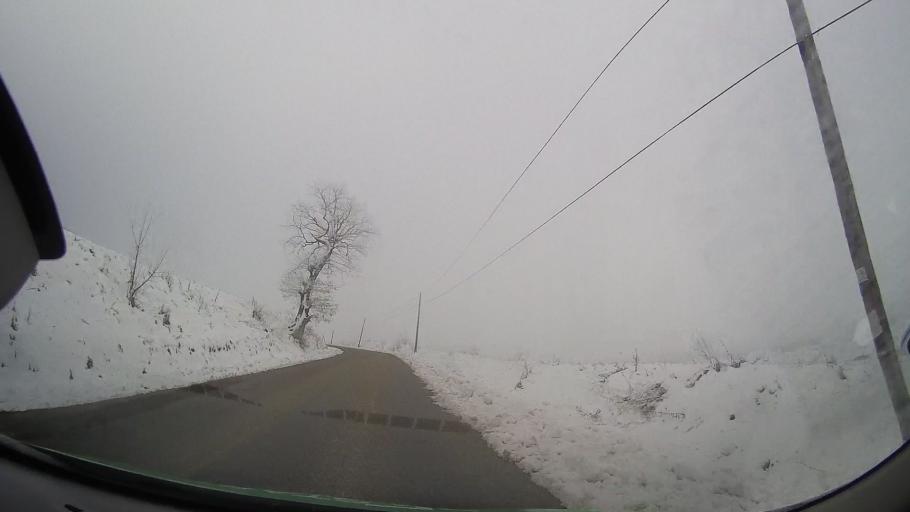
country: RO
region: Bacau
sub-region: Comuna Stanisesti
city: Stanisesti
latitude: 46.4119
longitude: 27.2699
